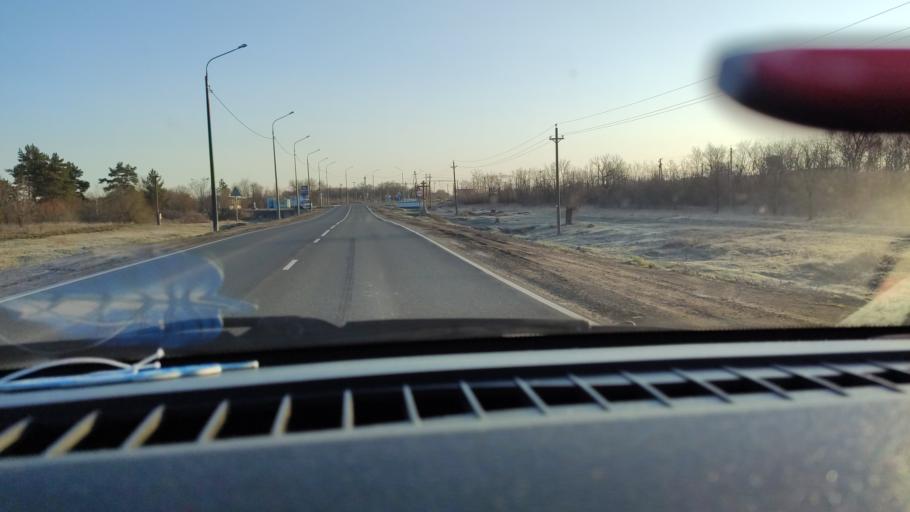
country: RU
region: Saratov
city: Sennoy
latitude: 52.1492
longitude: 46.9476
